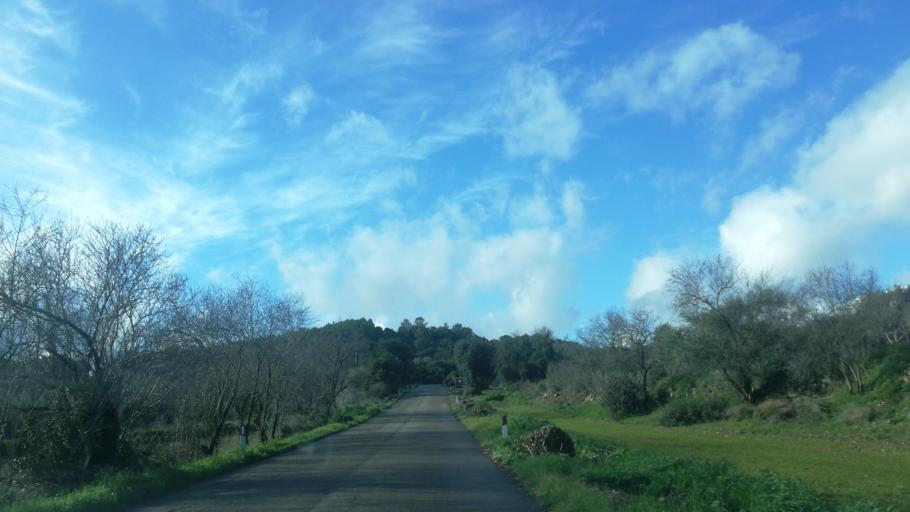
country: IT
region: Sardinia
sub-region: Provincia di Medio Campidano
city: Villanovaforru
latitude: 39.6336
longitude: 8.8598
